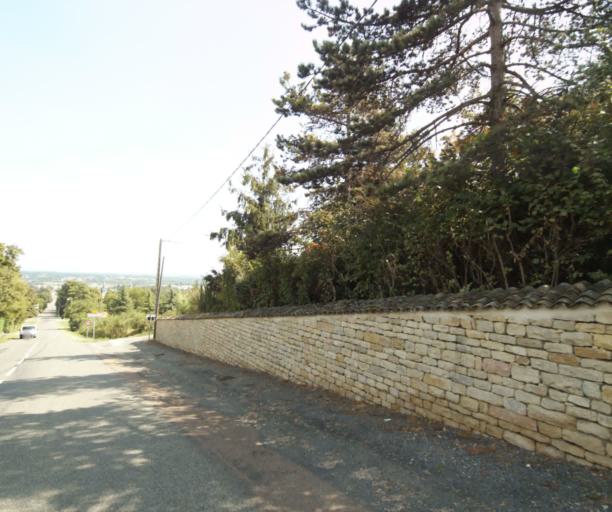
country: FR
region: Bourgogne
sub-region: Departement de Saone-et-Loire
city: Tournus
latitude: 46.5695
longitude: 4.8877
